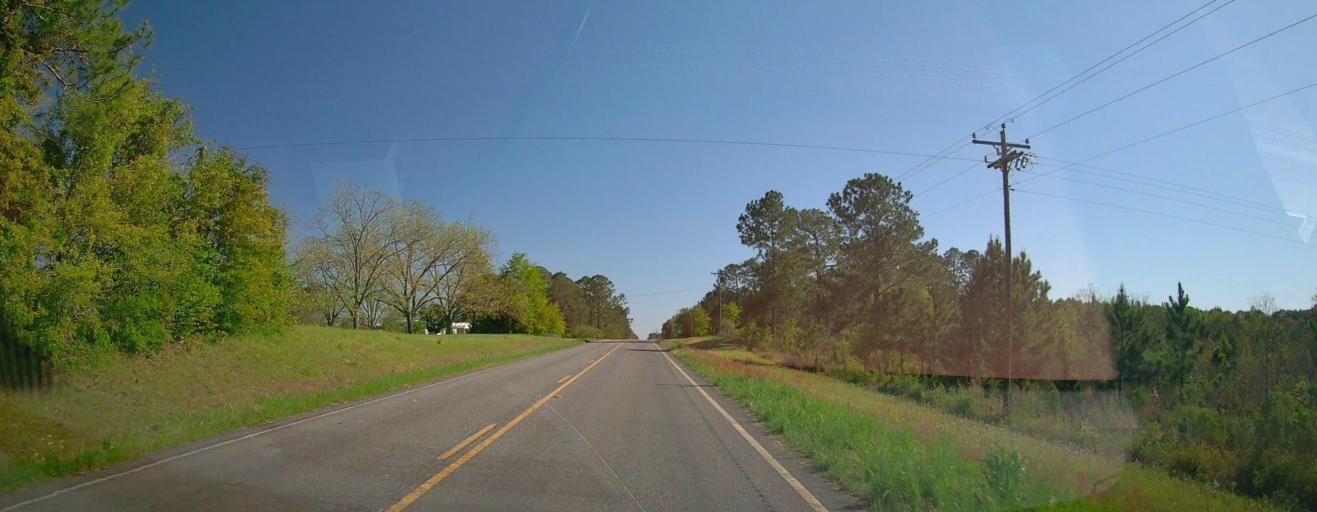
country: US
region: Georgia
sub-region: Wilcox County
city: Rochelle
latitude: 32.0668
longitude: -83.5036
